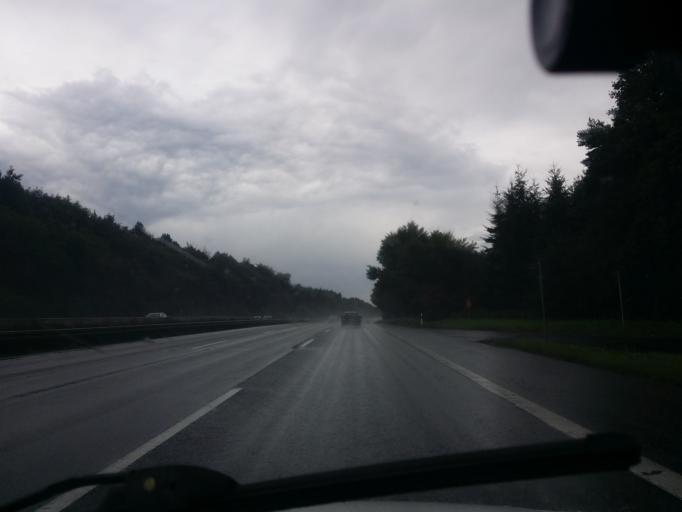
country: DE
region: Hesse
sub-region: Regierungsbezirk Kassel
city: Kirchheim
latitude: 50.8630
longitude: 9.5905
